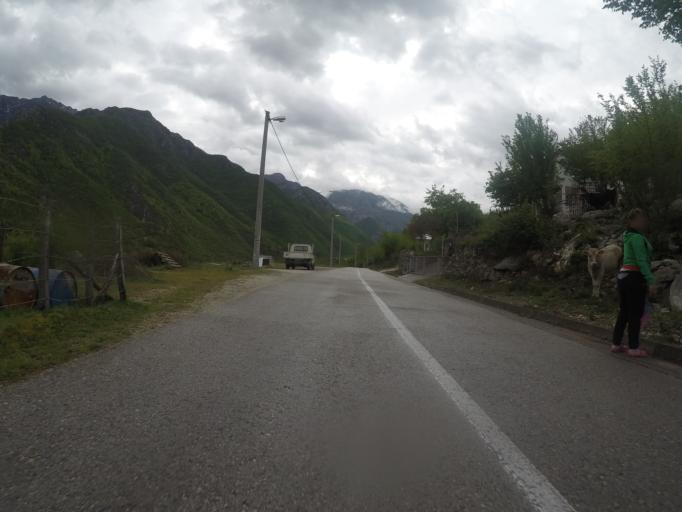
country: BA
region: Federation of Bosnia and Herzegovina
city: Siroki Brijeg
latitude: 43.5384
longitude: 17.6172
